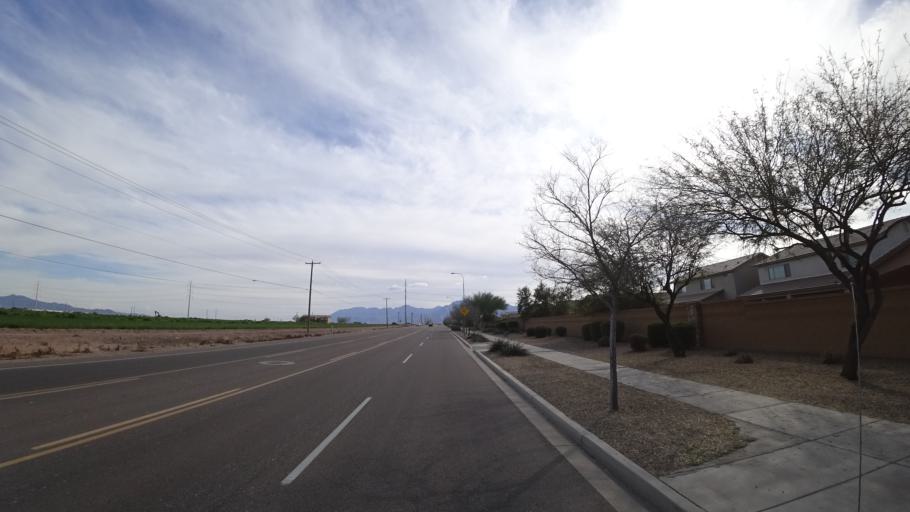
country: US
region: Arizona
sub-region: Maricopa County
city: Tolleson
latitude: 33.4094
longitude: -112.2726
